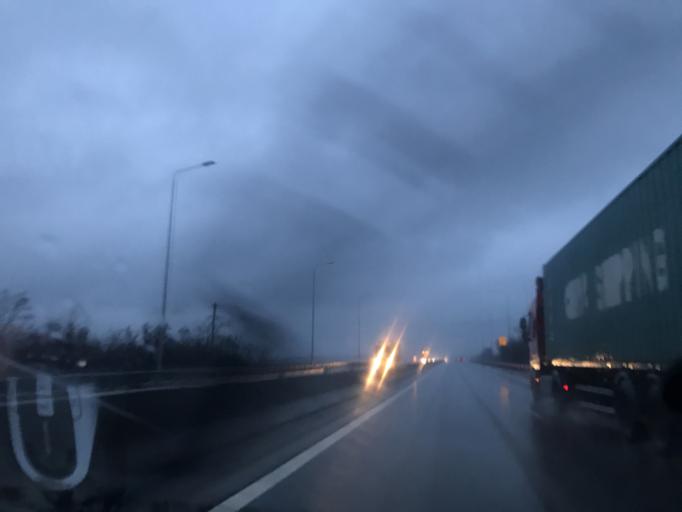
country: RU
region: Rostov
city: Samarskoye
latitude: 46.9423
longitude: 39.7117
